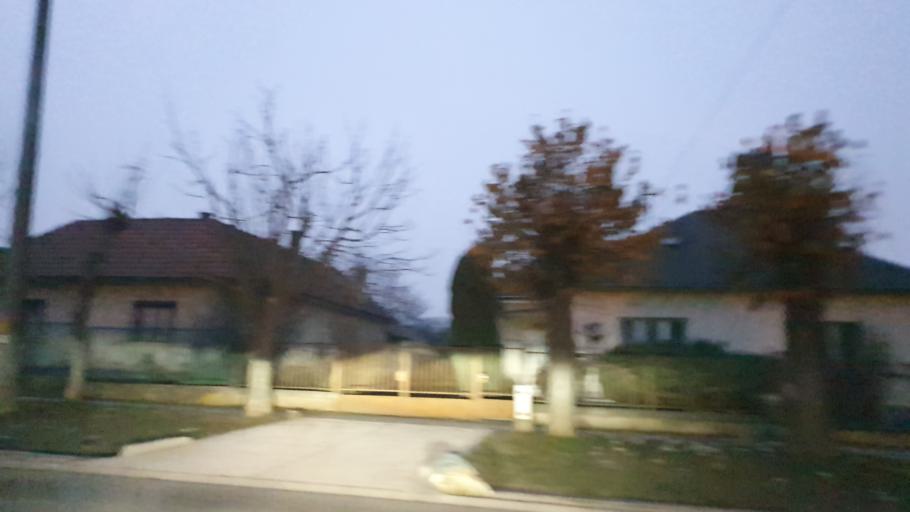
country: HU
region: Pest
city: Godollo
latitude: 47.6036
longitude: 19.3379
